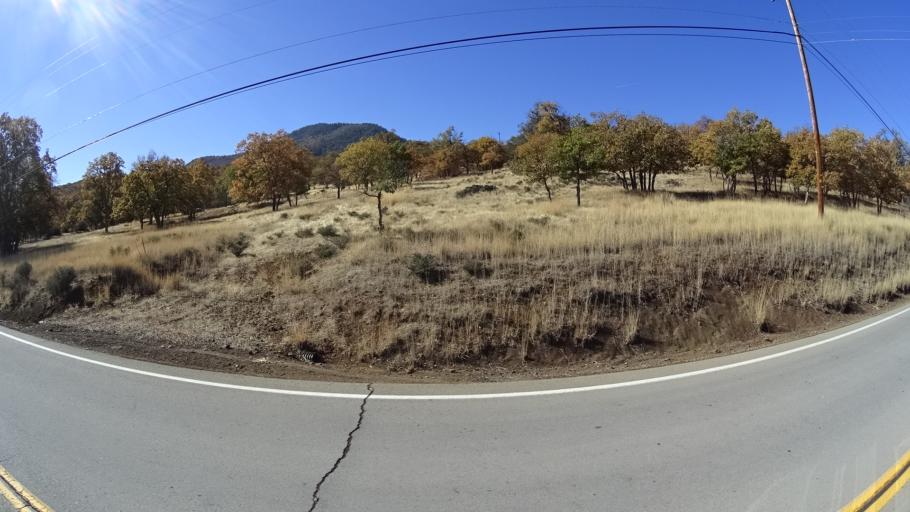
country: US
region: California
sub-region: Siskiyou County
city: Montague
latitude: 41.8889
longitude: -122.4939
